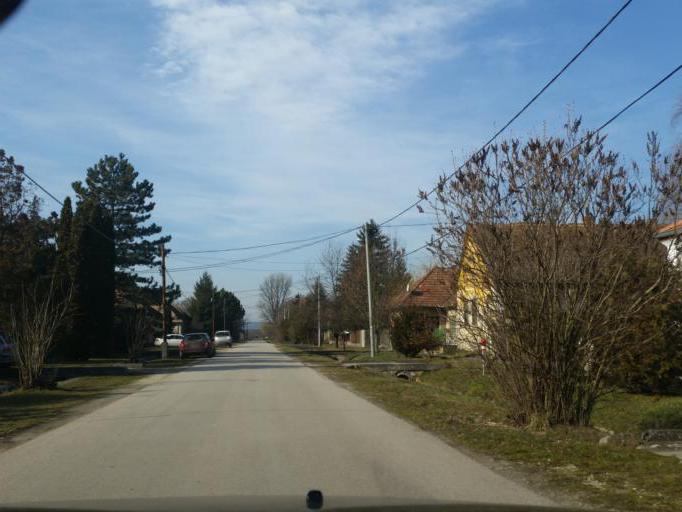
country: HU
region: Pest
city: Telki
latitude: 47.5554
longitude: 18.8000
